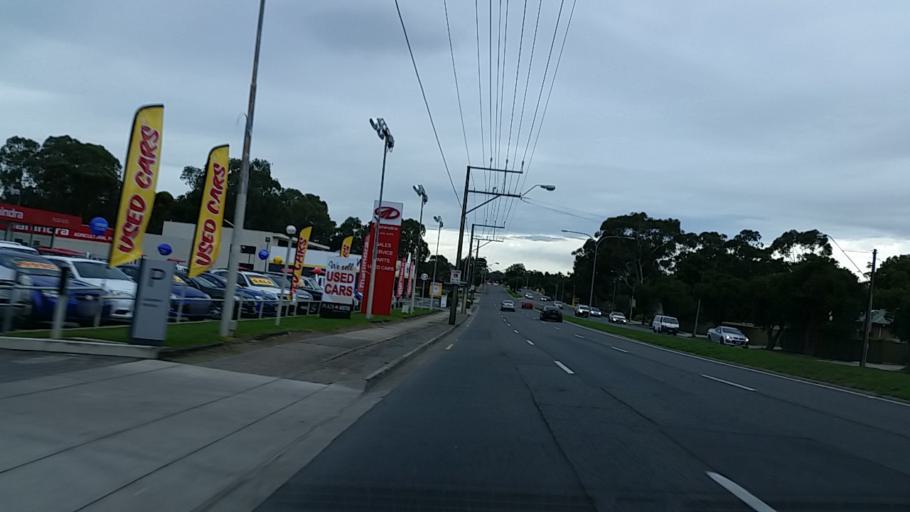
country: AU
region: South Australia
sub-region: Tea Tree Gully
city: Modbury
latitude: -34.8408
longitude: 138.6745
